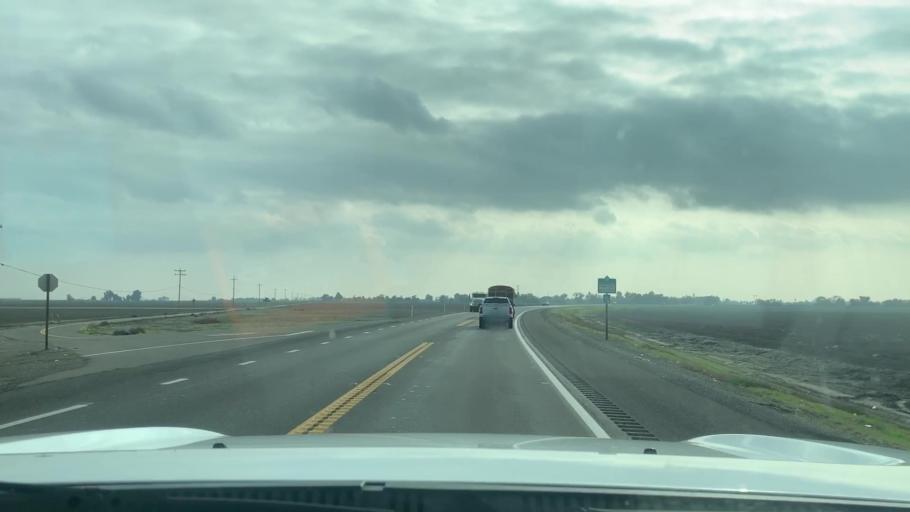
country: US
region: California
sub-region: Kings County
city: Stratford
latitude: 36.2068
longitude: -119.8165
